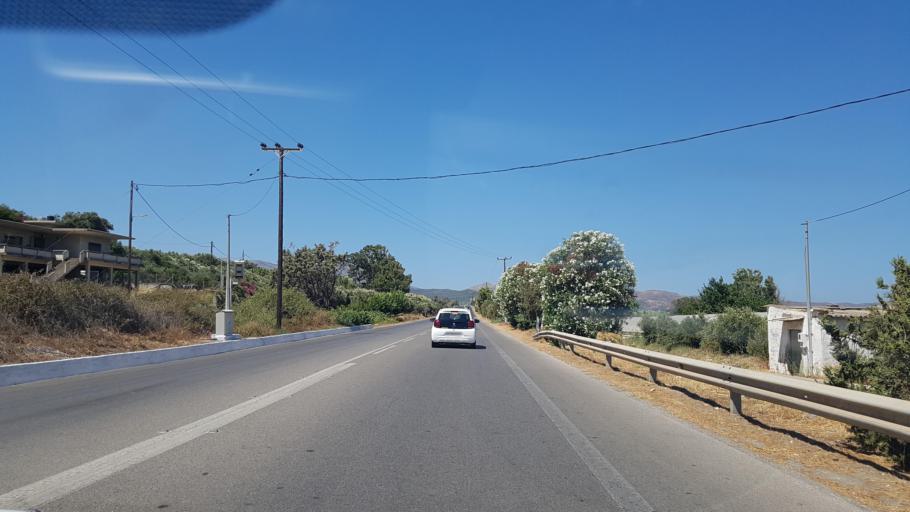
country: GR
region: Crete
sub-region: Nomos Chanias
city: Kissamos
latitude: 35.5016
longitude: 23.7116
